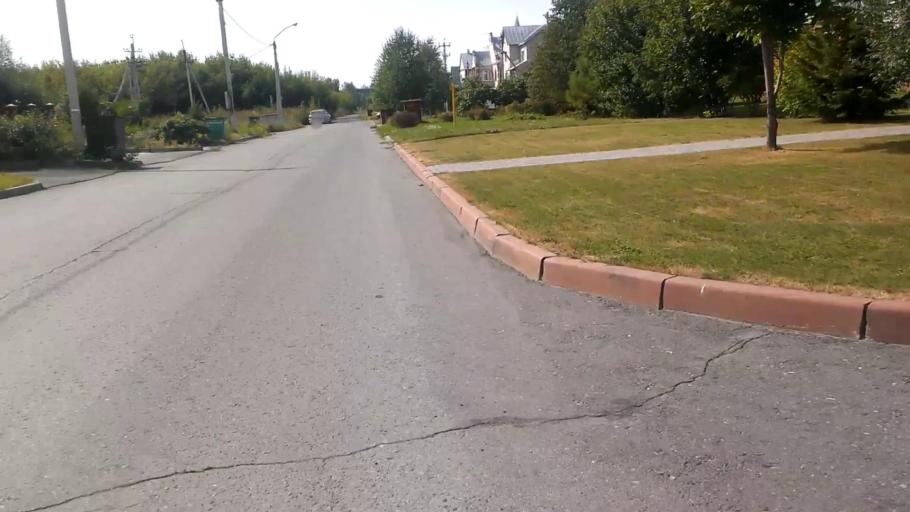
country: RU
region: Altai Krai
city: Novosilikatnyy
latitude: 53.3530
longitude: 83.6510
